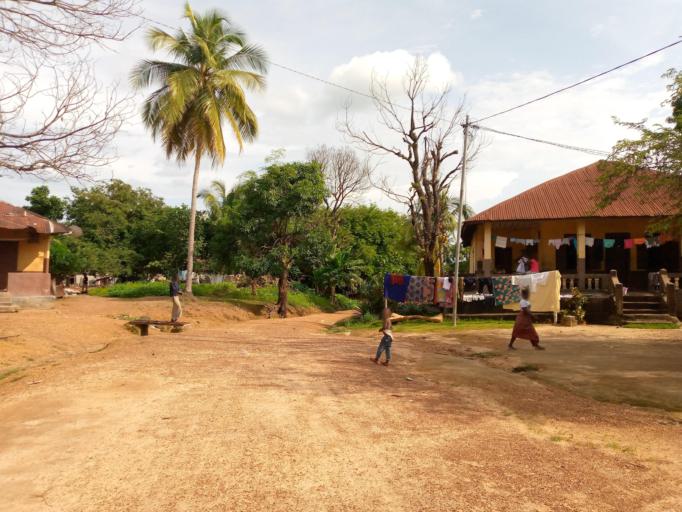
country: SL
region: Northern Province
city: Magburaka
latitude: 8.7205
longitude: -11.9552
